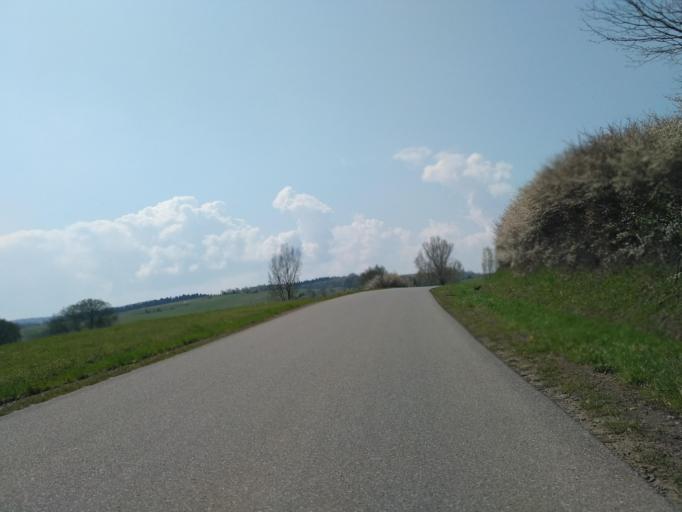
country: PL
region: Subcarpathian Voivodeship
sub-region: Powiat sanocki
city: Zarszyn
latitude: 49.5736
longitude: 22.0078
